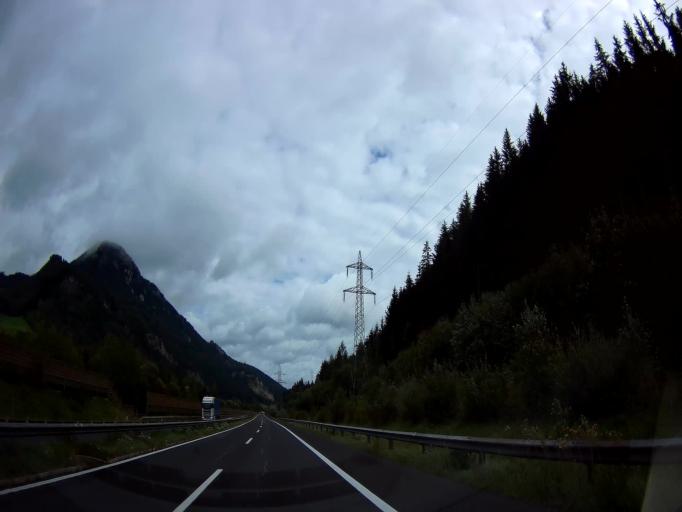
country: AT
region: Styria
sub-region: Politischer Bezirk Leoben
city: Mautern in Steiermark
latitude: 47.3950
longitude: 14.8344
